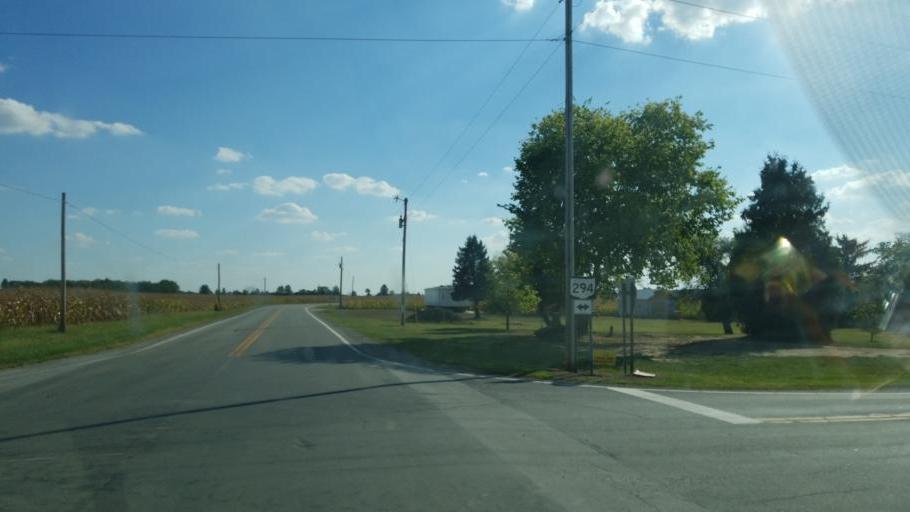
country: US
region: Ohio
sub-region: Wyandot County
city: Upper Sandusky
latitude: 40.7377
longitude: -83.3689
